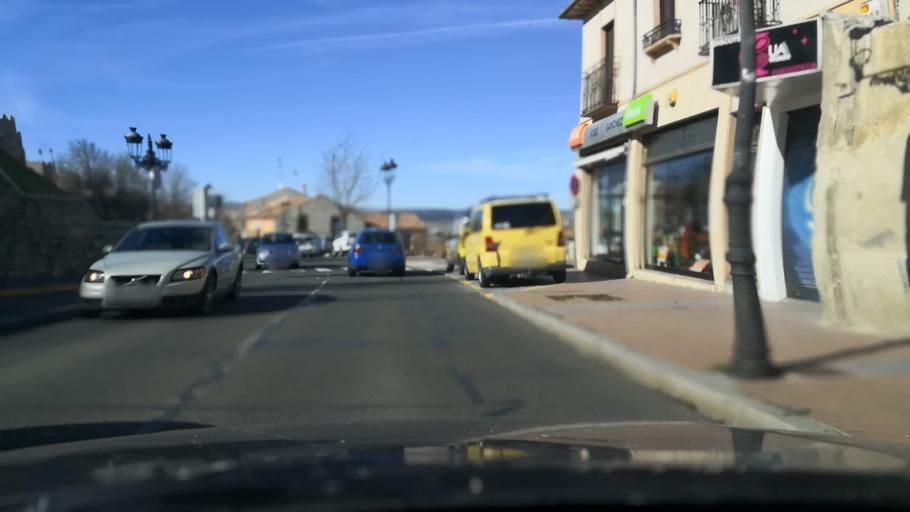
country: ES
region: Castille and Leon
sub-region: Provincia de Avila
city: Avila
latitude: 40.6586
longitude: -4.6970
